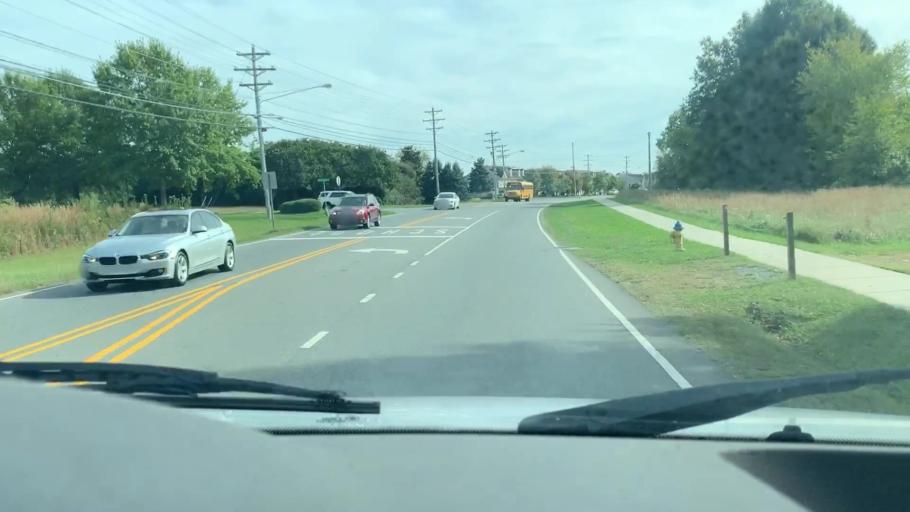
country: US
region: North Carolina
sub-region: Mecklenburg County
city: Cornelius
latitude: 35.4676
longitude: -80.8894
